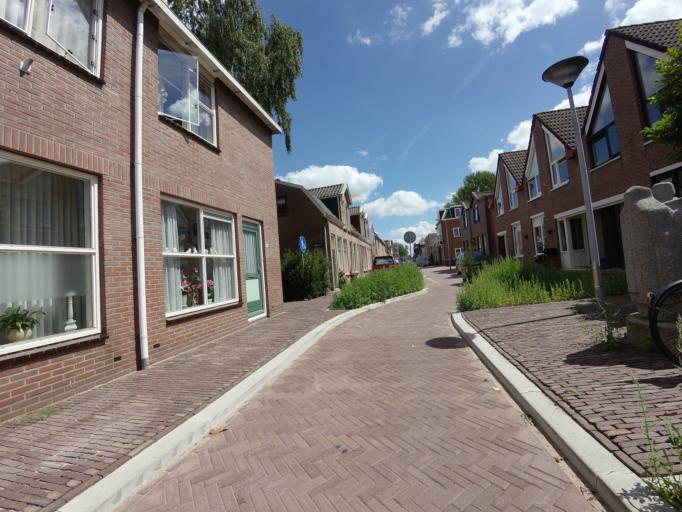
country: NL
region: North Holland
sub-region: Gemeente Zaanstad
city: Zaandam
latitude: 52.4382
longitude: 4.8203
